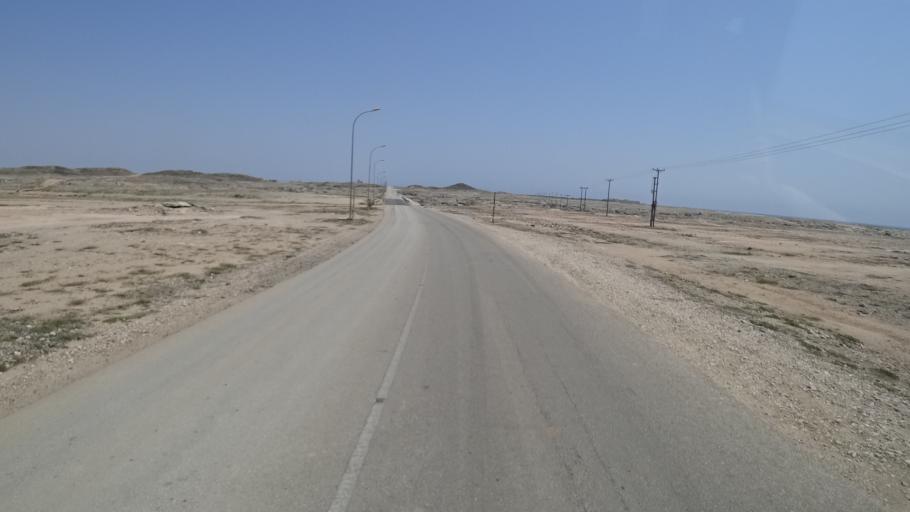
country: OM
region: Zufar
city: Salalah
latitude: 16.9724
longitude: 54.7191
